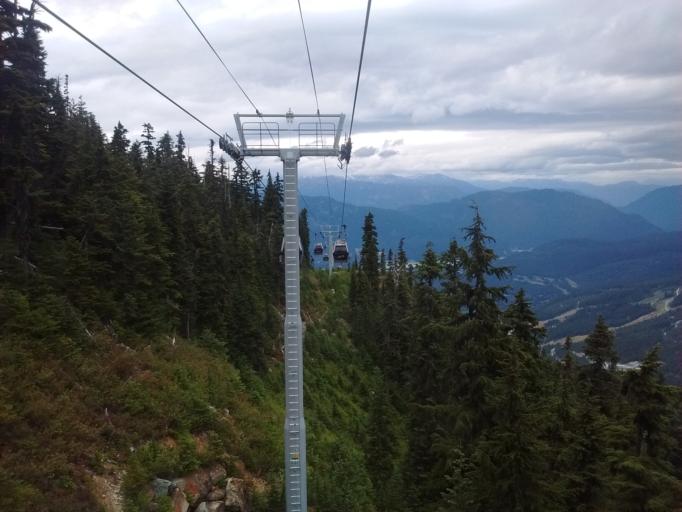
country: CA
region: British Columbia
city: Whistler
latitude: 50.0820
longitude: -122.9488
